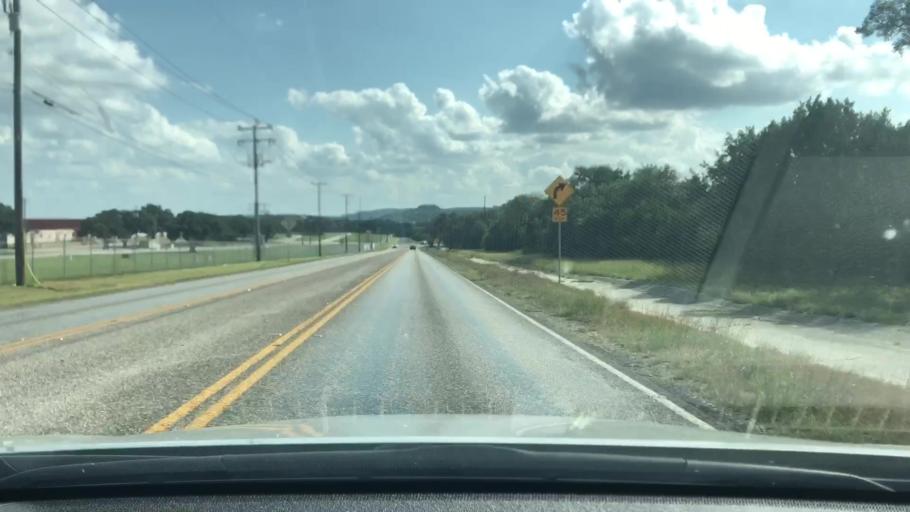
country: US
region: Texas
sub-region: Bexar County
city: Cross Mountain
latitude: 29.6827
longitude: -98.6316
